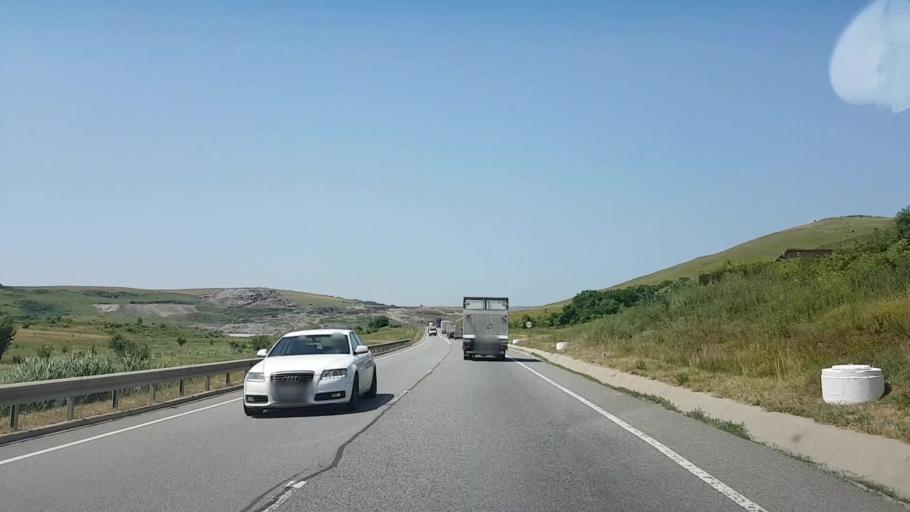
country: RO
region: Cluj
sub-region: Comuna Apahida
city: Dezmir
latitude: 46.7569
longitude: 23.6987
